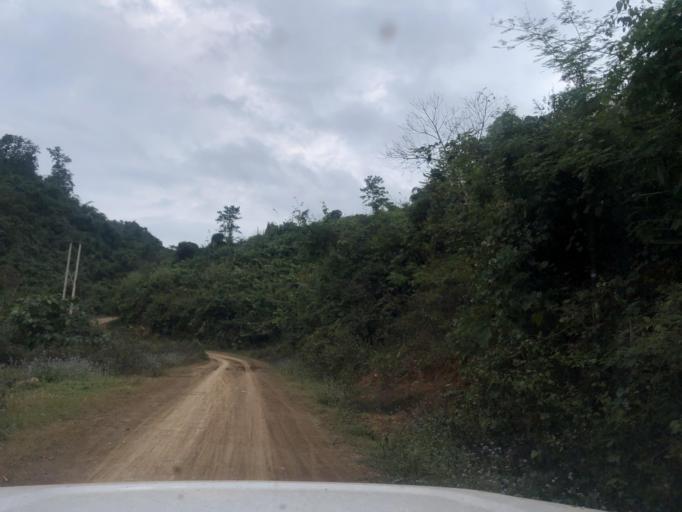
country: LA
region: Phongsali
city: Khoa
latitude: 21.3050
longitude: 102.5825
